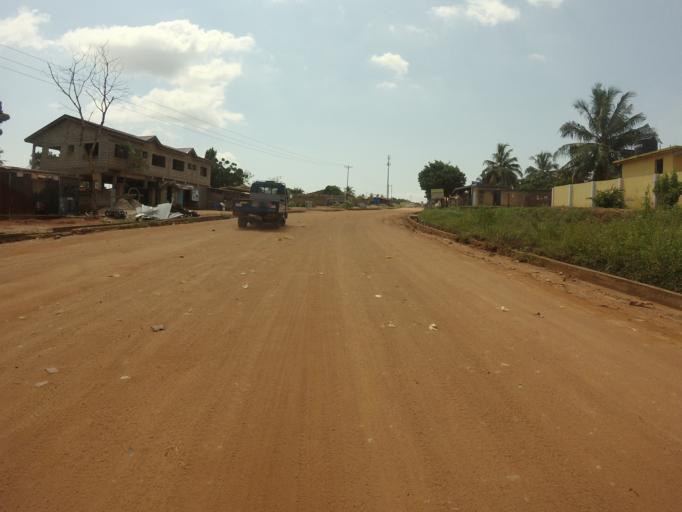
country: GH
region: Greater Accra
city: Gbawe
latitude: 5.6199
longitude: -0.3071
